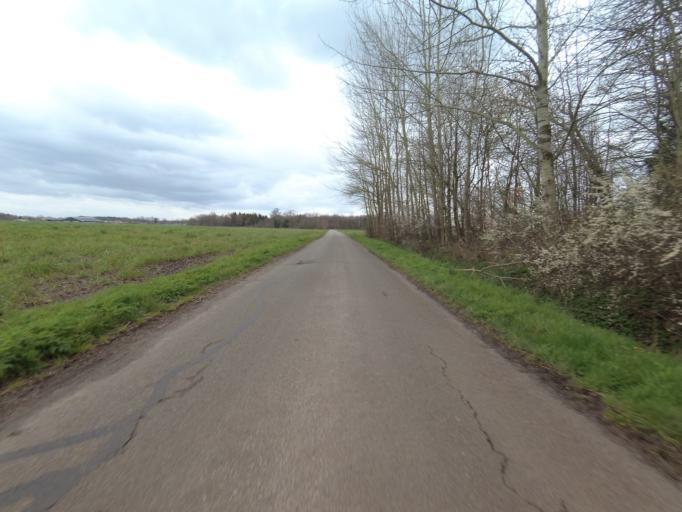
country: NL
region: Gelderland
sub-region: Gemeente Barneveld
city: Zwartebroek
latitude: 52.1595
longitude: 5.4870
